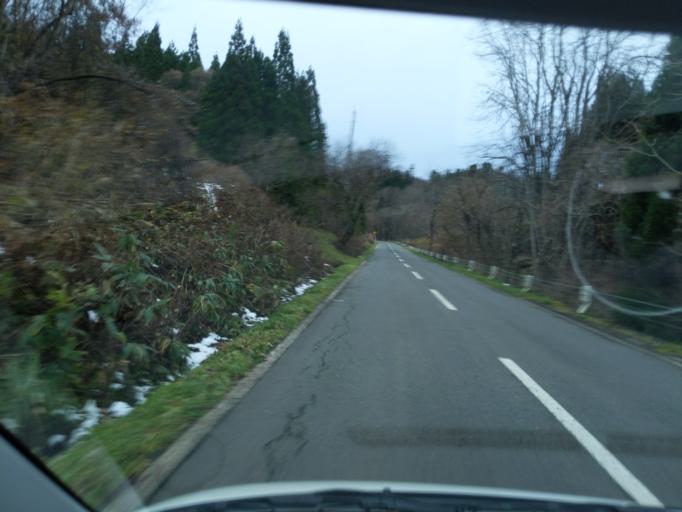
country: JP
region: Iwate
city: Tono
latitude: 39.1608
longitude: 141.3651
